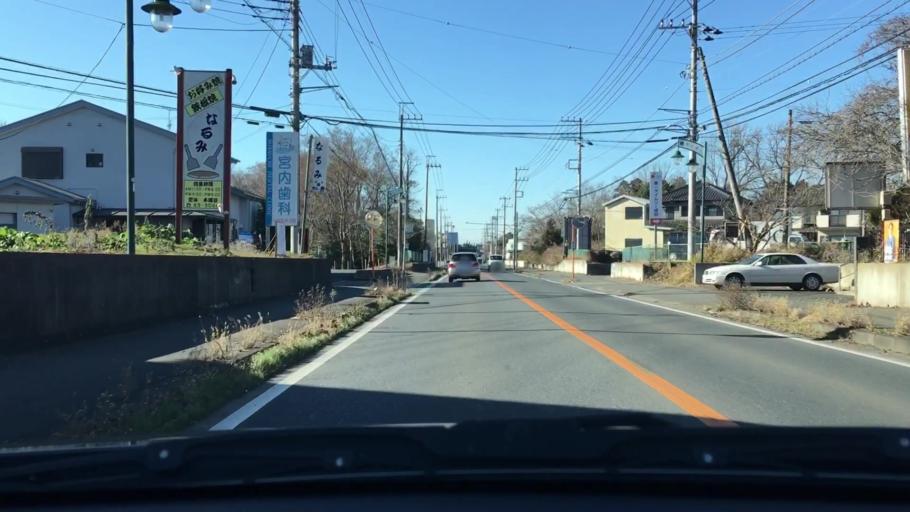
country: JP
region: Chiba
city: Narita
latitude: 35.7290
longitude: 140.3480
